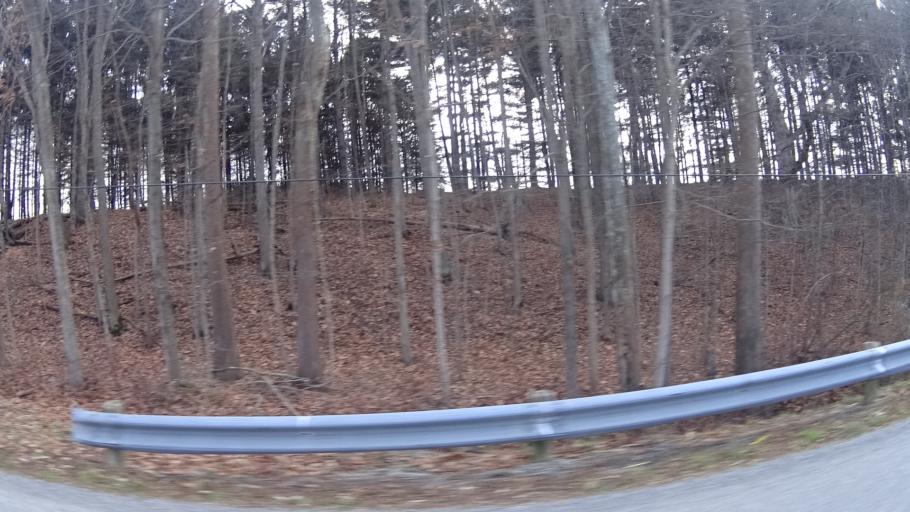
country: US
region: Ohio
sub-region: Lorain County
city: Camden
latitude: 41.1488
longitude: -82.3092
